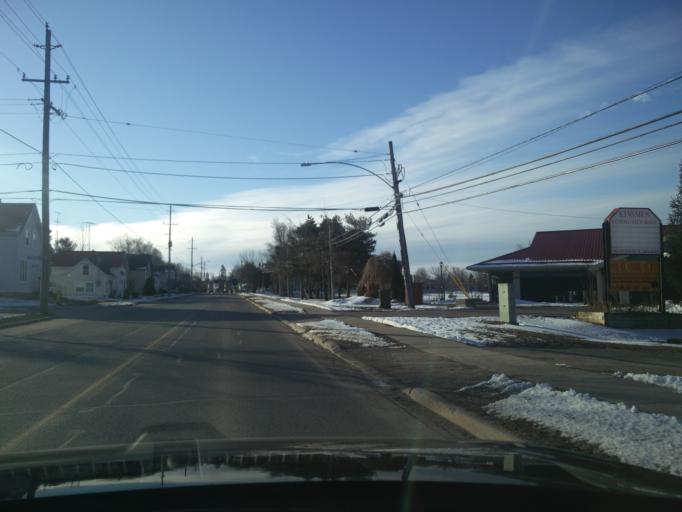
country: CA
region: Ontario
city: Gananoque
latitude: 44.3335
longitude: -76.1669
